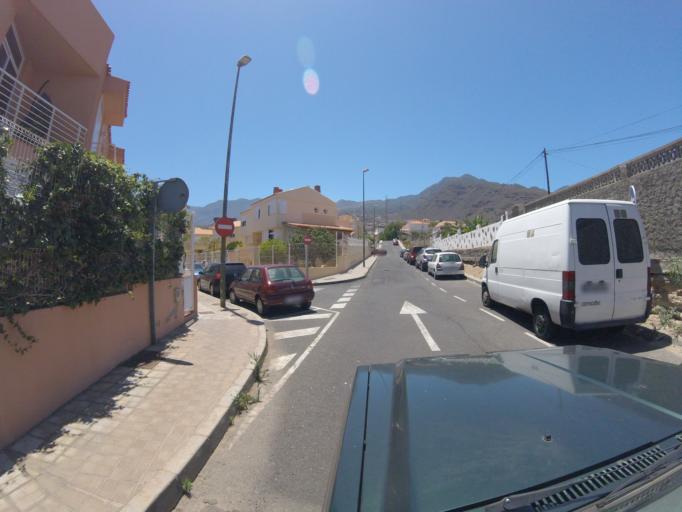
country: ES
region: Canary Islands
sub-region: Provincia de Santa Cruz de Tenerife
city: Candelaria
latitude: 28.3588
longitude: -16.3737
